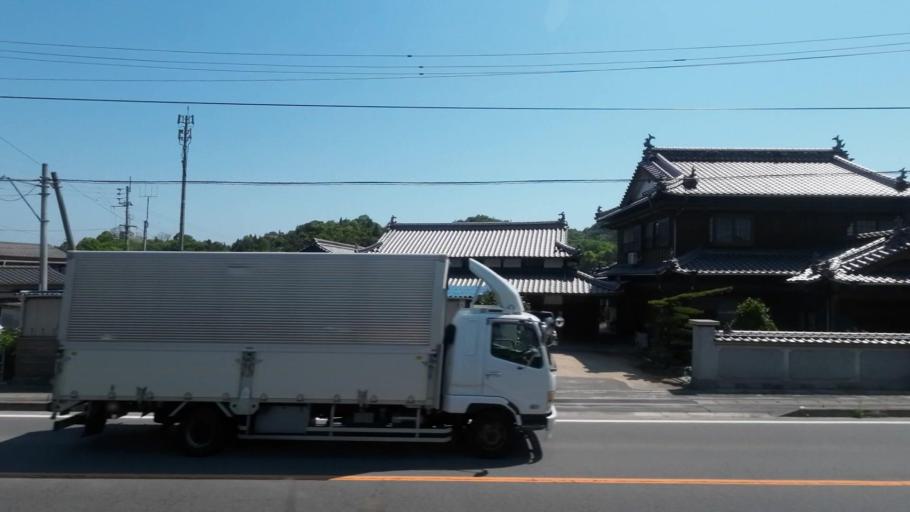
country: JP
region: Ehime
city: Saijo
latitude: 33.9842
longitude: 133.0528
